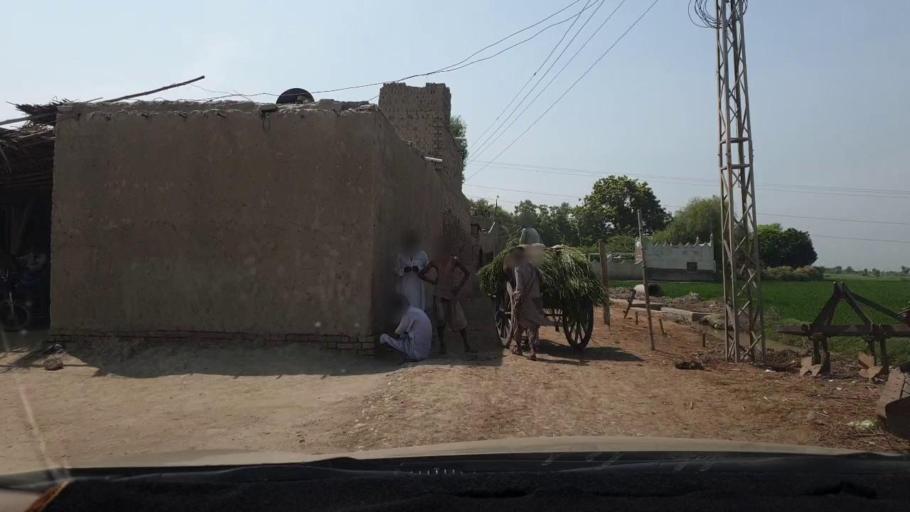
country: PK
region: Sindh
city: Naudero
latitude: 27.6478
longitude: 68.2609
